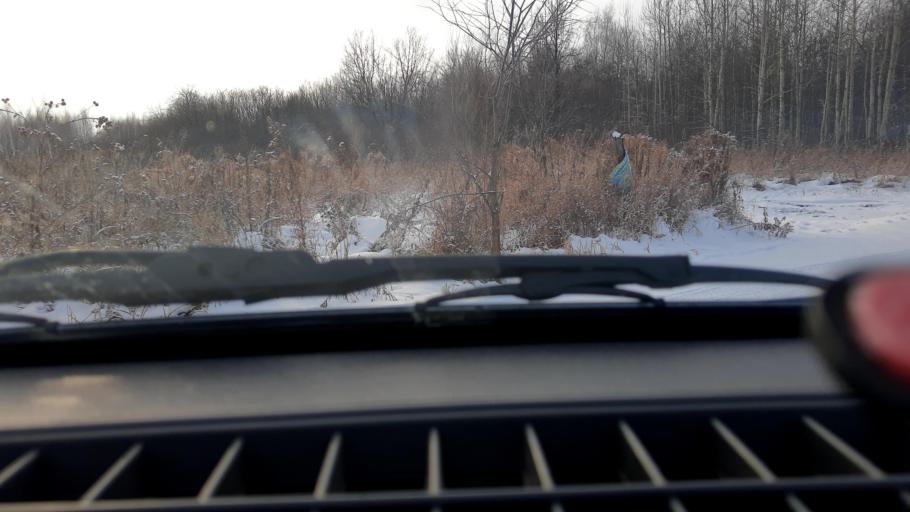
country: RU
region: Bashkortostan
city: Iglino
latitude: 54.7970
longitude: 56.3457
